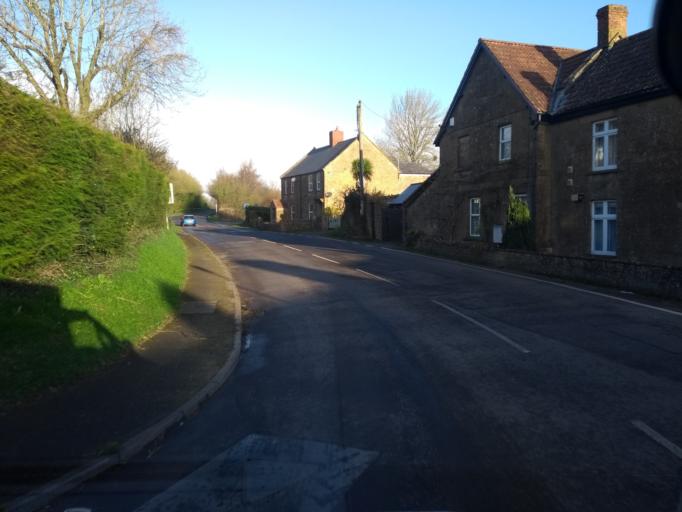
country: GB
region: England
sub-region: Somerset
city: Stoke-sub-Hamdon
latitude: 50.9601
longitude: -2.7510
